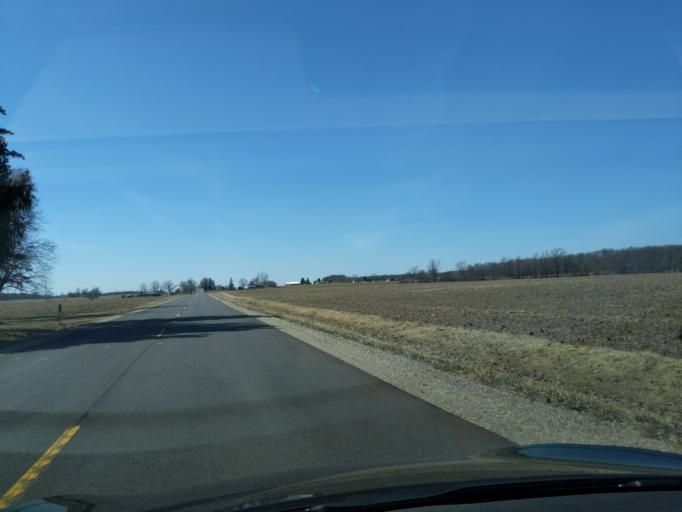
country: US
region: Michigan
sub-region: Eaton County
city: Grand Ledge
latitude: 42.7266
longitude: -84.8830
